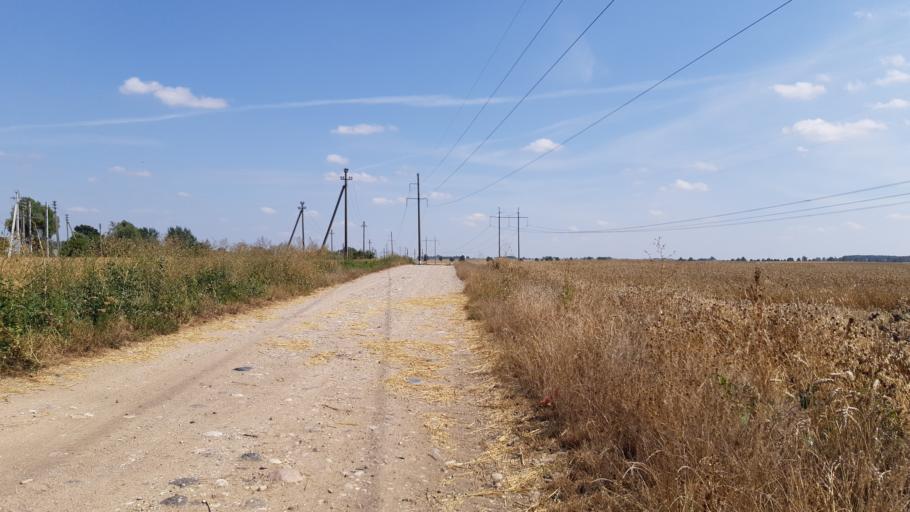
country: LT
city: Virbalis
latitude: 54.6189
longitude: 22.8104
